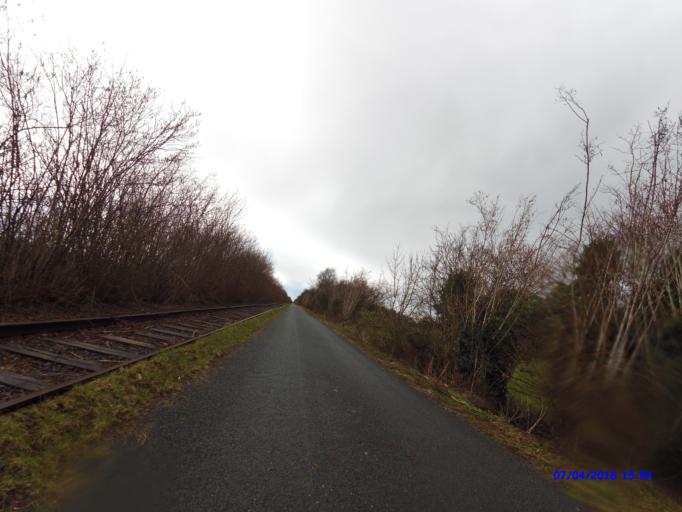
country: IE
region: Leinster
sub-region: An Iarmhi
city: Athlone
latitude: 53.4168
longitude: -7.8687
